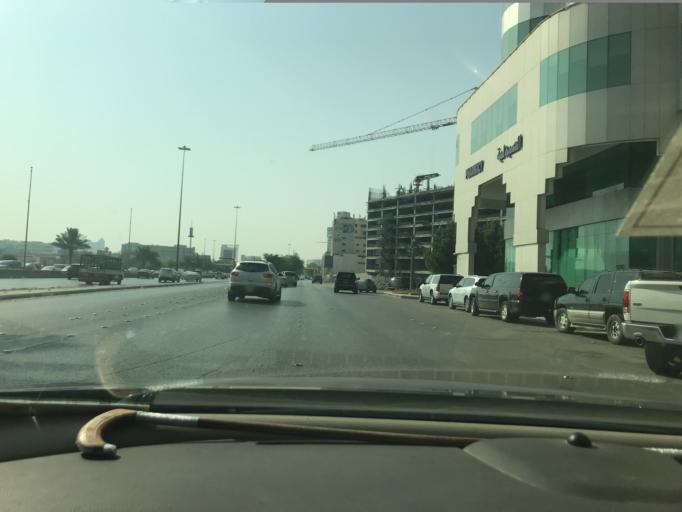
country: SA
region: Ar Riyad
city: Riyadh
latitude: 24.6580
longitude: 46.7008
